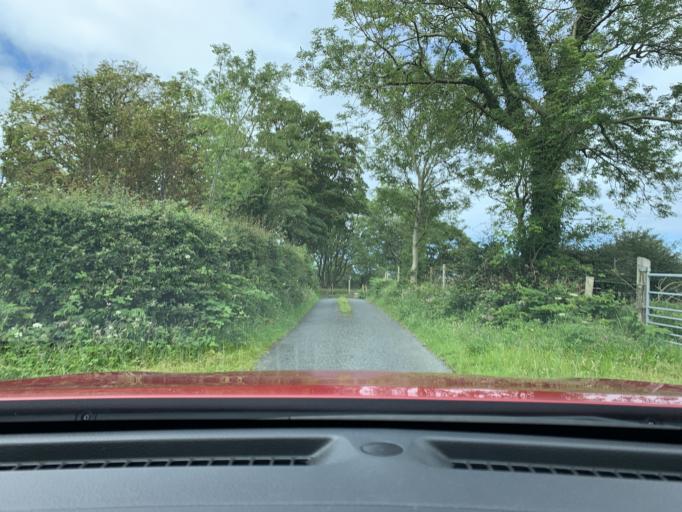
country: IE
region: Connaught
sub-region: Sligo
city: Sligo
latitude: 54.3801
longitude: -8.5050
